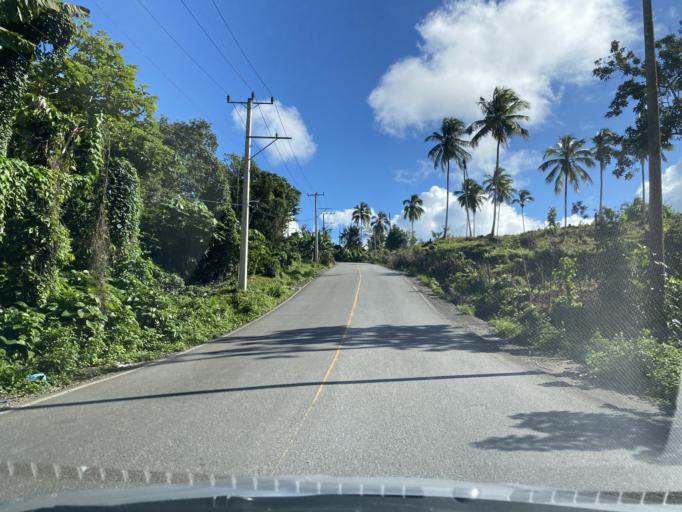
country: DO
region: Samana
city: Sanchez
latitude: 19.2560
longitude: -69.5779
